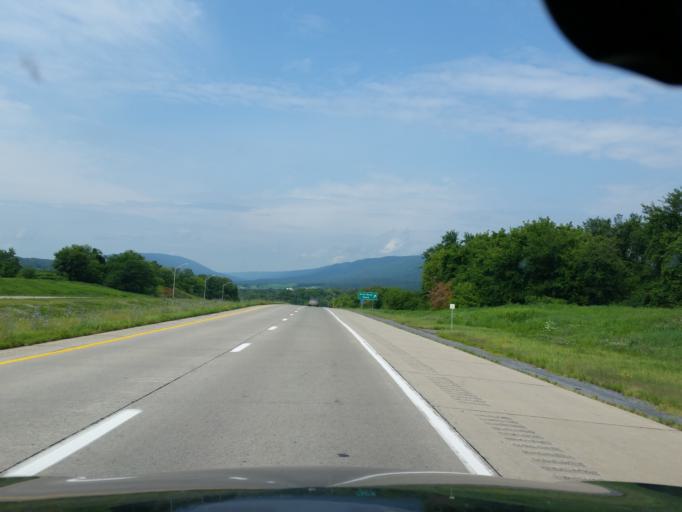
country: US
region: Pennsylvania
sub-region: Juniata County
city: Mifflintown
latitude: 40.6044
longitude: -77.4030
